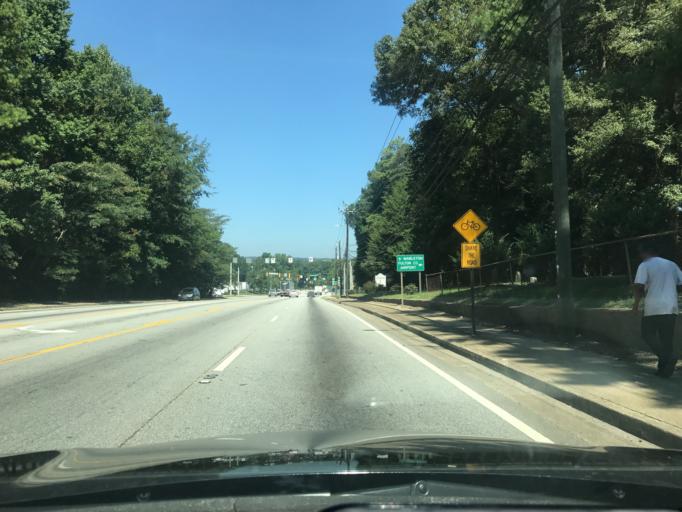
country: US
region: Georgia
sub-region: Cobb County
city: Vinings
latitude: 33.7885
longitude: -84.4950
